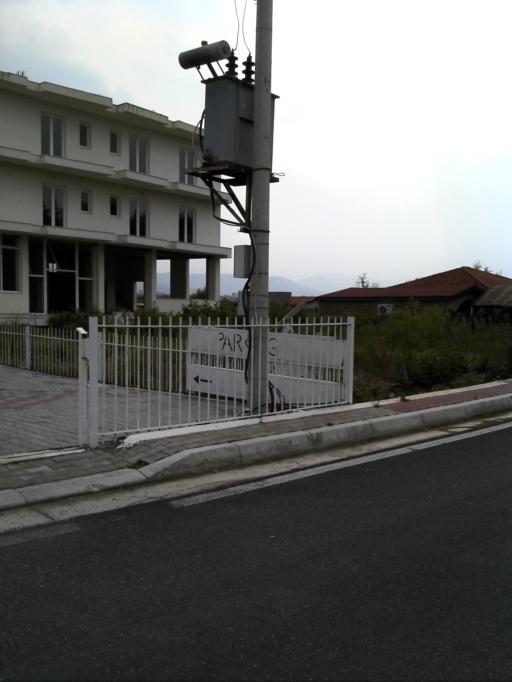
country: AL
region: Lezhe
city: Shengjin
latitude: 41.7896
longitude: 19.6031
